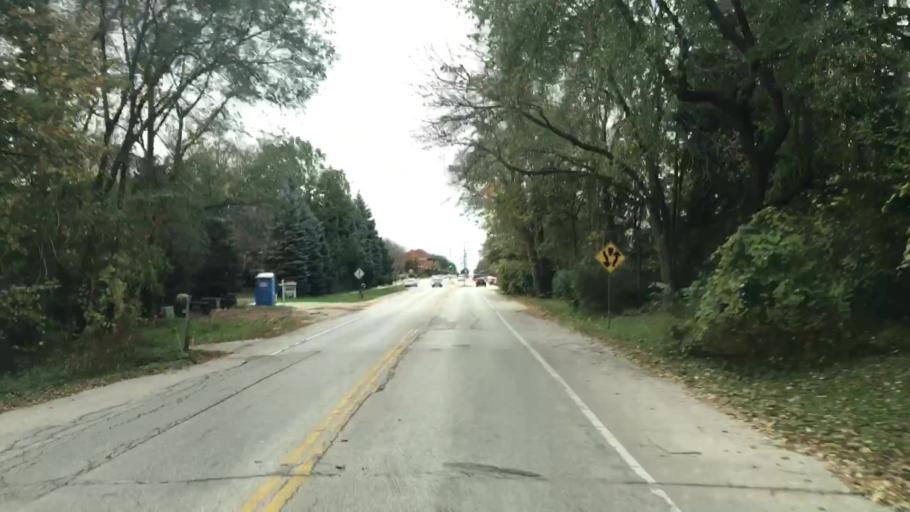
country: US
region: Wisconsin
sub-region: Waukesha County
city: Brookfield
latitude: 43.0633
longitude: -88.1261
